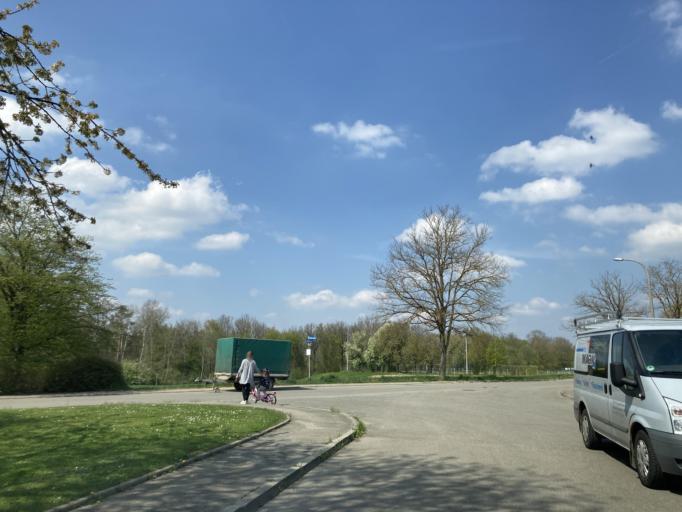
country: DE
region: Baden-Wuerttemberg
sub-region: Tuebingen Region
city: Kusterdingen
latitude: 48.5238
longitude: 9.1122
